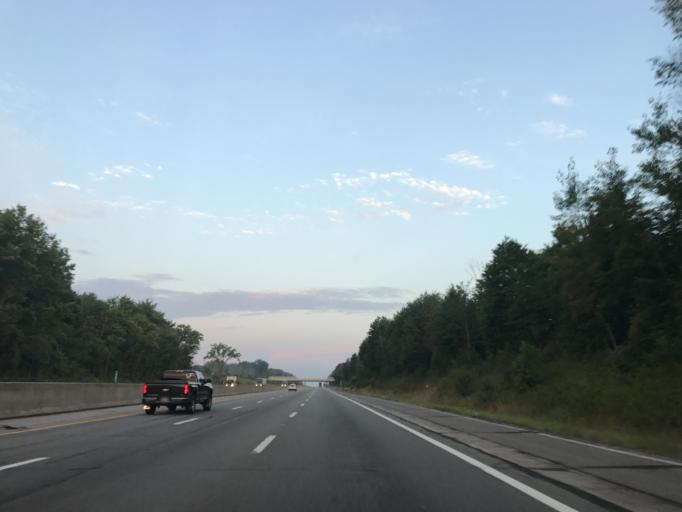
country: US
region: Ohio
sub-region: Portage County
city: Hiram
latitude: 41.2435
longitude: -81.1549
